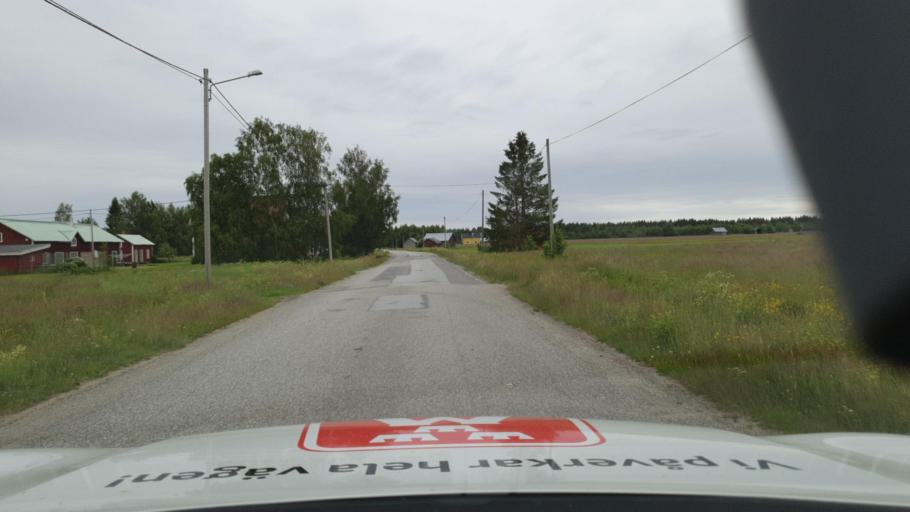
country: SE
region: Vaesterbotten
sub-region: Nordmalings Kommun
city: Nordmaling
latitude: 63.5427
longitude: 19.3938
